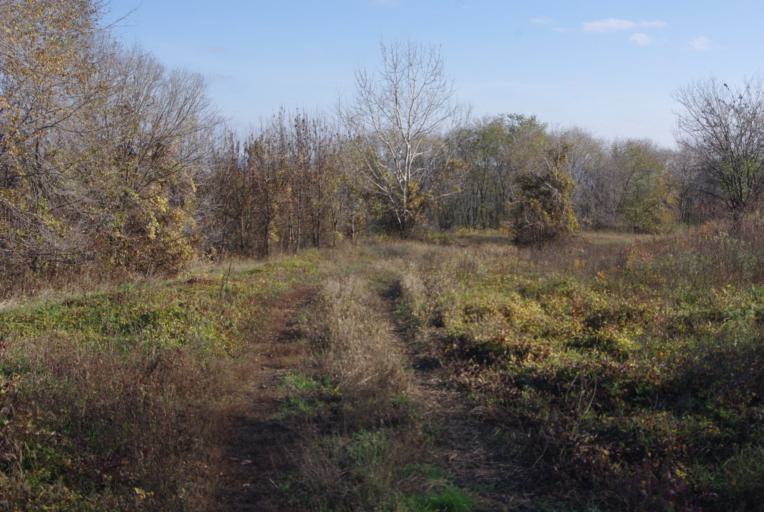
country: HU
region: Pest
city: Urom
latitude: 47.5877
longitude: 19.0366
